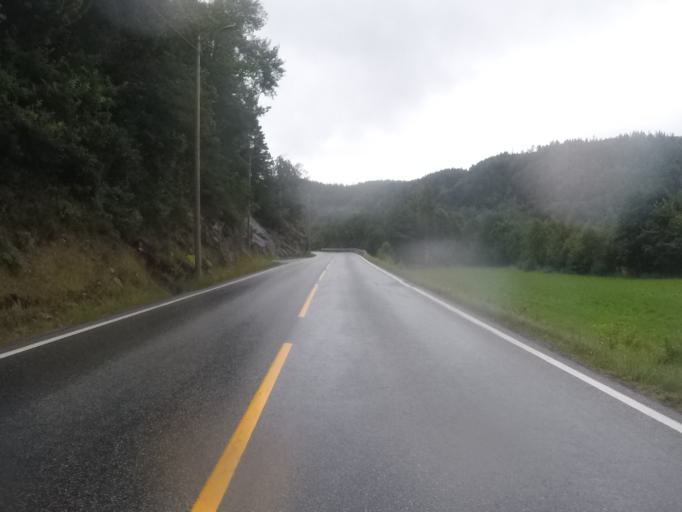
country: NO
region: Vest-Agder
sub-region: Songdalen
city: Nodeland
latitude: 58.1787
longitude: 7.8157
